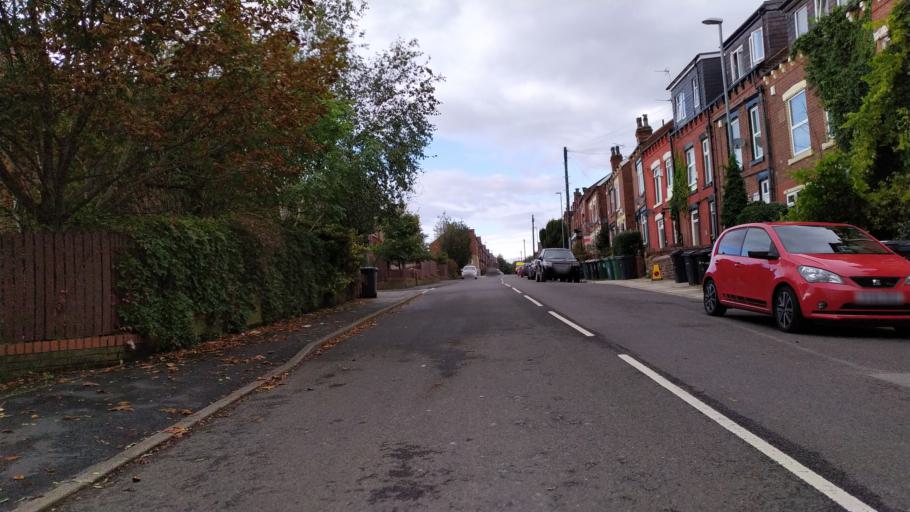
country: GB
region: England
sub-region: City and Borough of Leeds
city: Chapel Allerton
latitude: 53.8162
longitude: -1.5497
